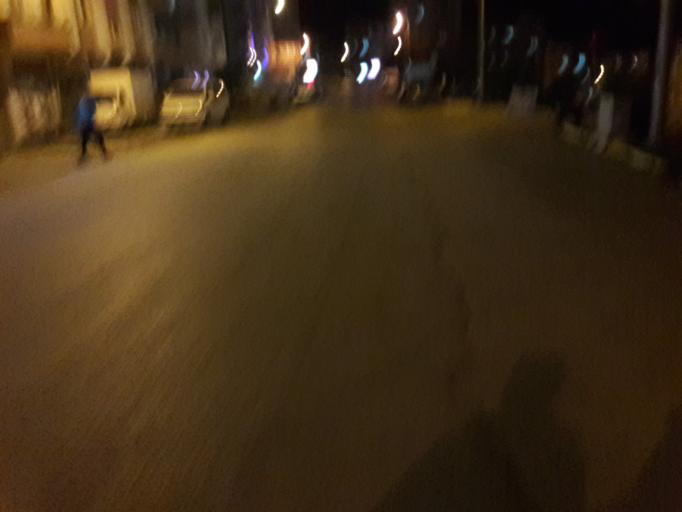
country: TR
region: Sinop
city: Sinop
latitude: 42.0219
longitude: 35.1341
